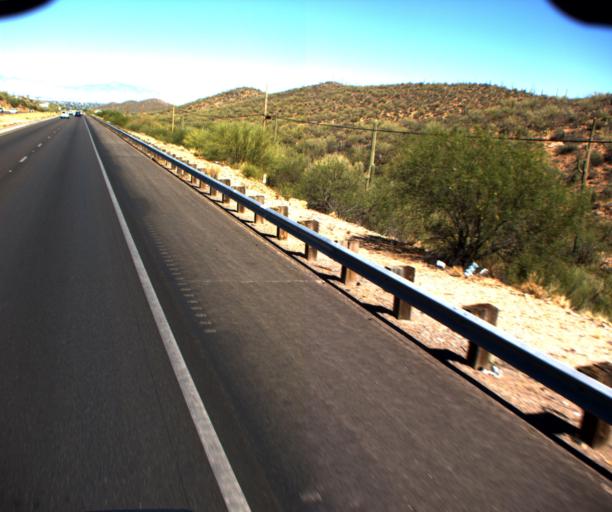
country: US
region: Arizona
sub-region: Pima County
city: Drexel Heights
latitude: 32.1774
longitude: -111.0415
